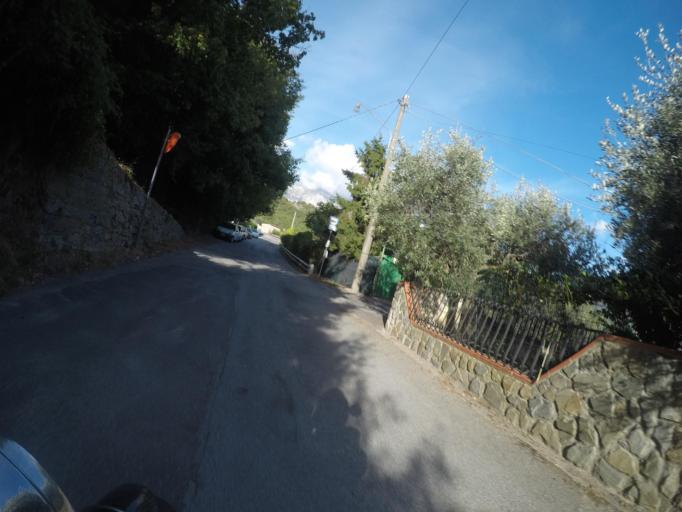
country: IT
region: Tuscany
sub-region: Provincia di Massa-Carrara
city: Carrara
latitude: 44.0867
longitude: 10.0925
